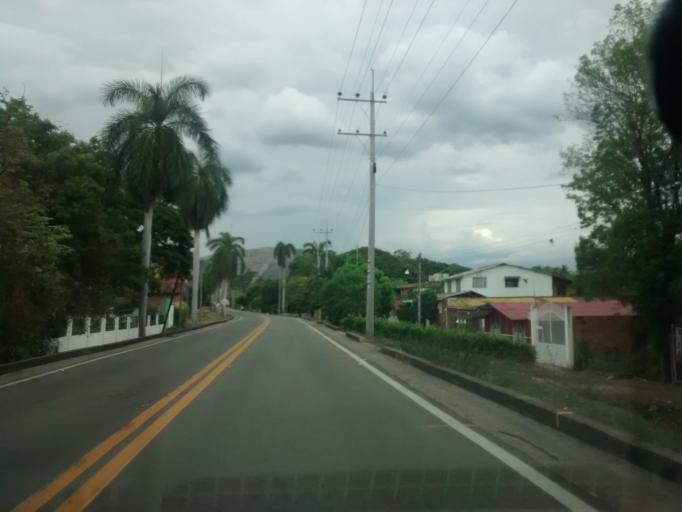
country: CO
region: Cundinamarca
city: Tocaima
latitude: 4.4515
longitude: -74.6506
